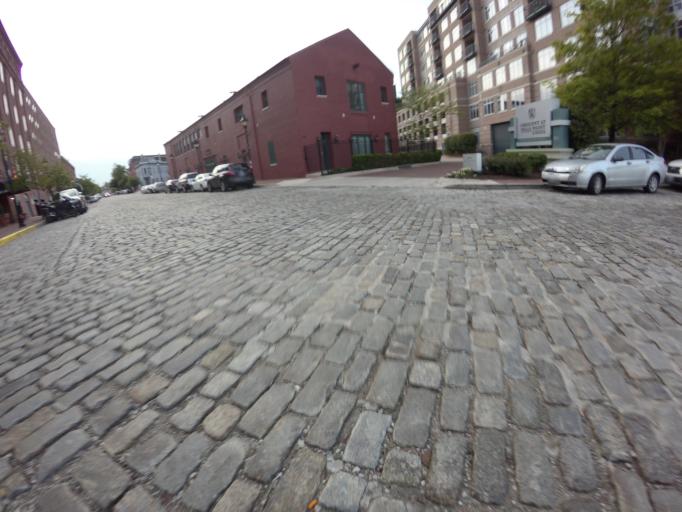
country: US
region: Maryland
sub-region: City of Baltimore
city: Baltimore
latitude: 39.2802
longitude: -76.5885
